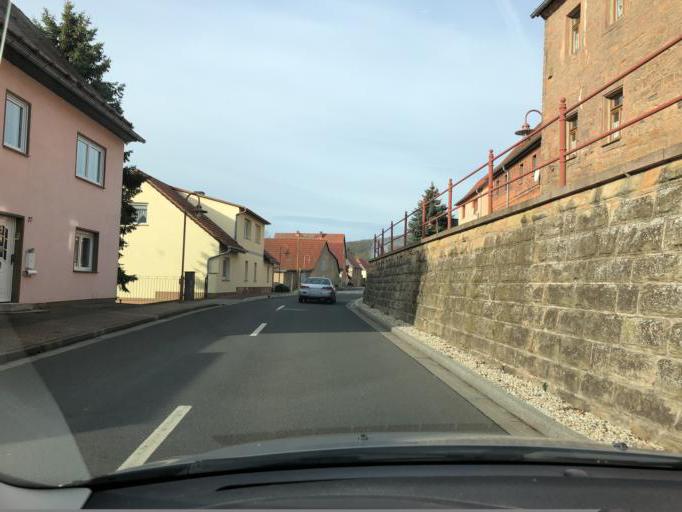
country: DE
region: Saxony-Anhalt
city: Bad Bibra
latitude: 51.2235
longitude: 11.6102
